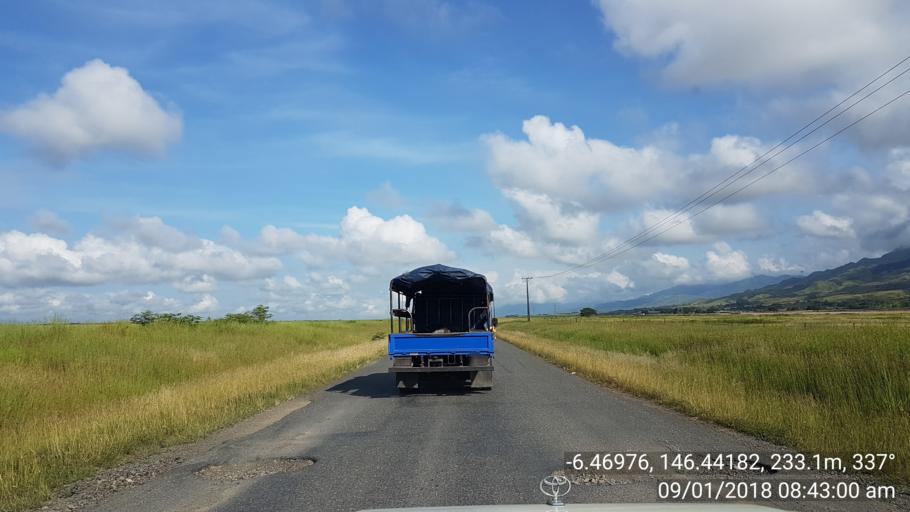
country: PG
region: Morobe
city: Lae
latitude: -6.4696
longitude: 146.4423
